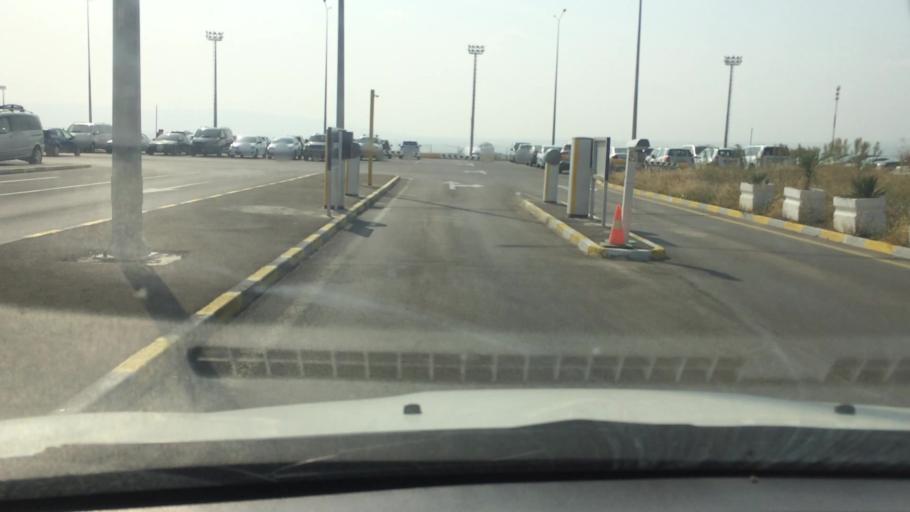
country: GE
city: Didi Lilo
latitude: 41.6718
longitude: 44.9625
